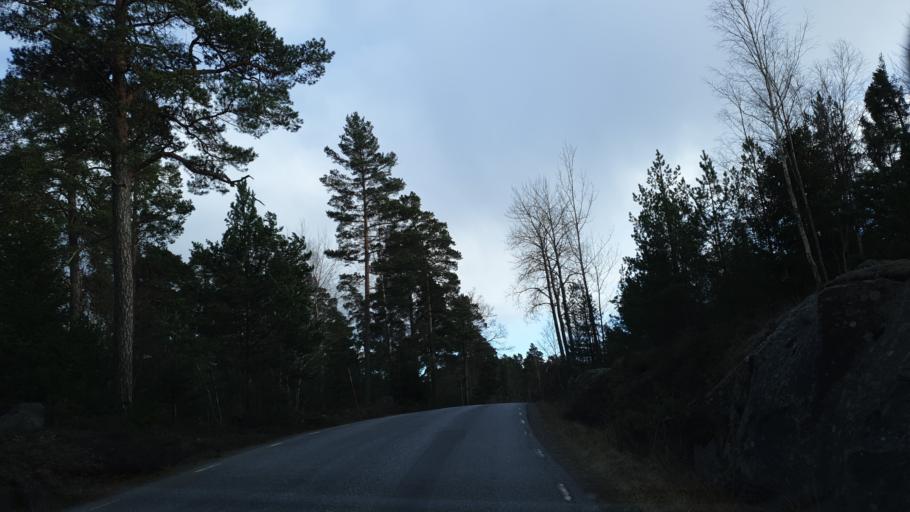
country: SE
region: Stockholm
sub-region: Varmdo Kommun
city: Holo
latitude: 59.3542
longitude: 18.7023
